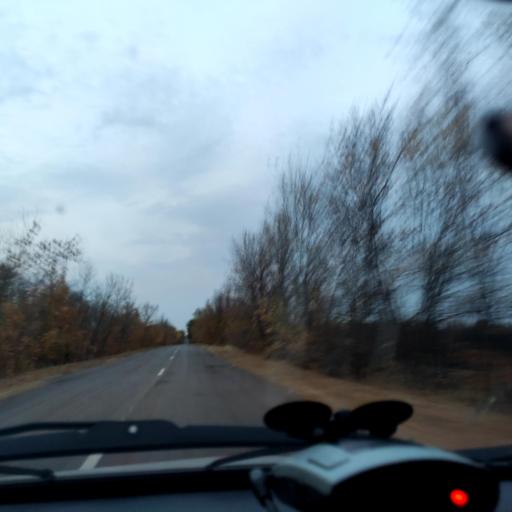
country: RU
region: Belgorod
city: Krasnoye
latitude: 51.2261
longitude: 38.8344
